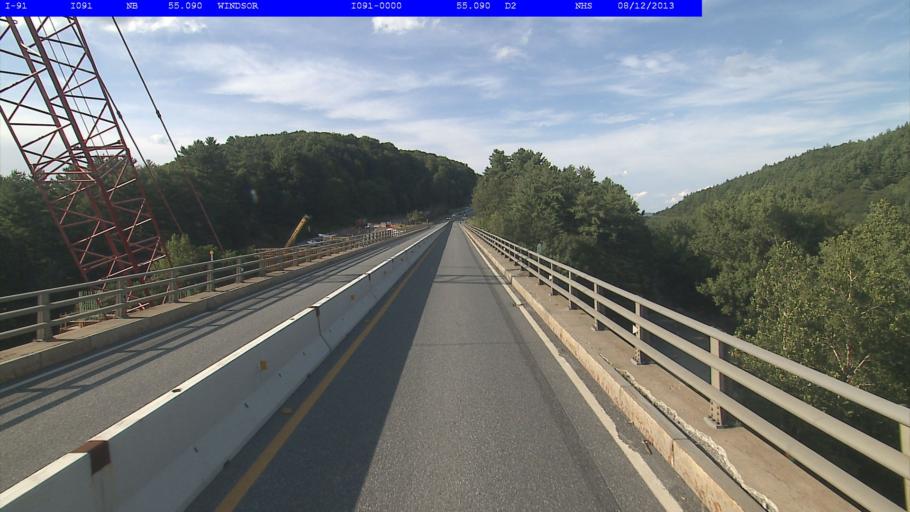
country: US
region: Vermont
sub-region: Windsor County
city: Windsor
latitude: 43.4531
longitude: -72.4068
